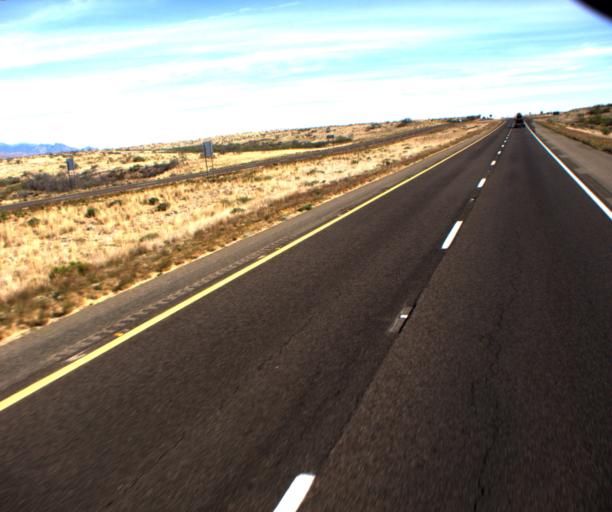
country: US
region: Arizona
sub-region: Cochise County
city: Willcox
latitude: 32.3887
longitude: -109.6652
